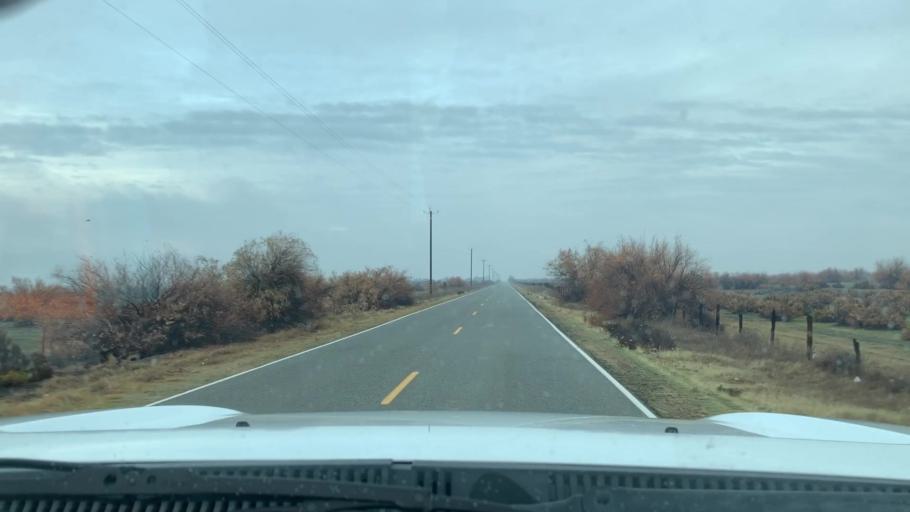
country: US
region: California
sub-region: Kern County
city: Lost Hills
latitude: 35.7054
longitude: -119.5796
